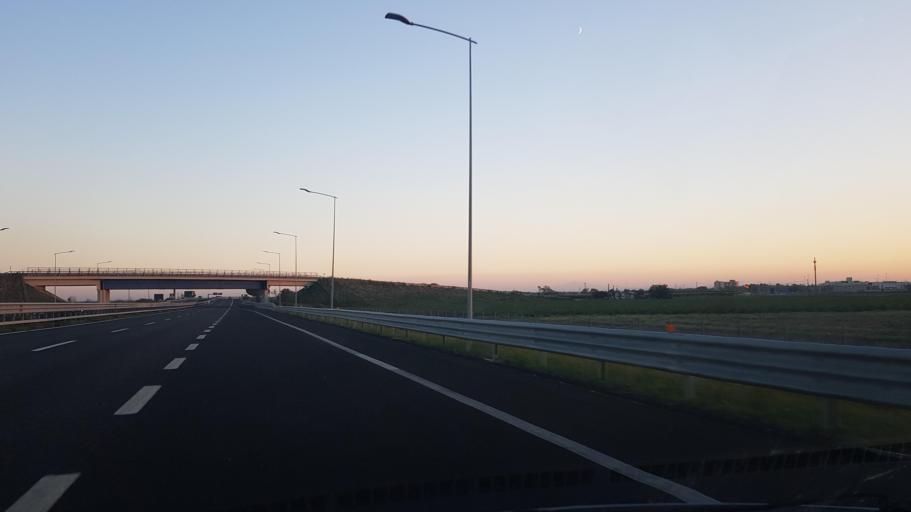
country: IT
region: Apulia
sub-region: Provincia di Foggia
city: Carapelle
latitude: 41.4268
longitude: 15.6588
